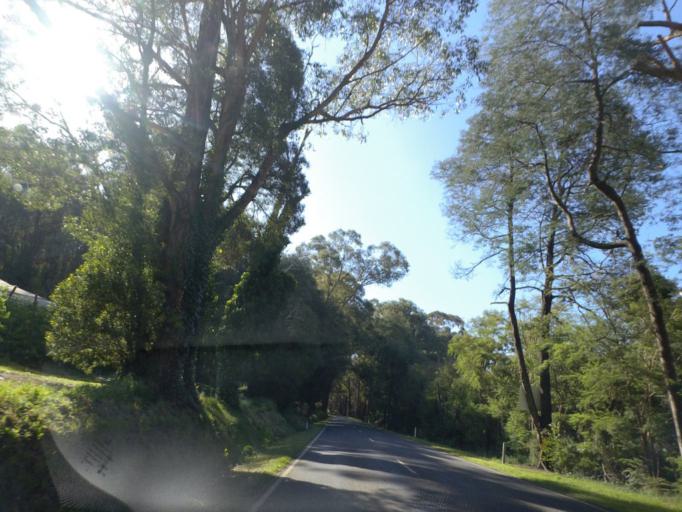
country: AU
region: Victoria
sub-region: Yarra Ranges
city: Yarra Junction
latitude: -37.8387
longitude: 145.6783
